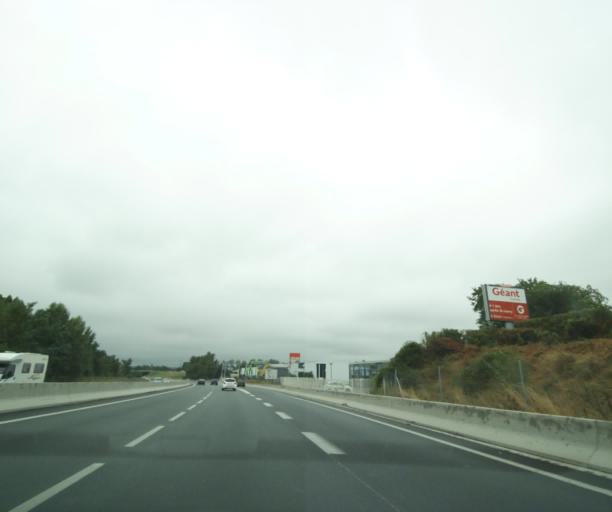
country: FR
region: Midi-Pyrenees
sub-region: Departement du Tarn
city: Albi
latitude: 43.9269
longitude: 2.1727
